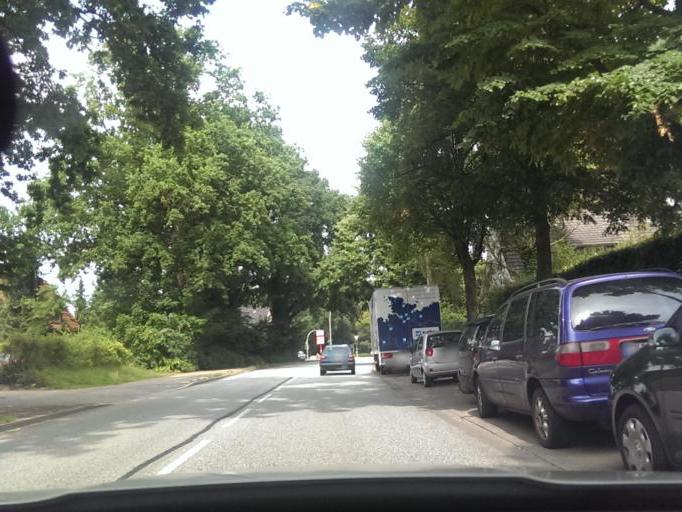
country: DE
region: Hamburg
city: Poppenbuettel
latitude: 53.6624
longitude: 10.0762
